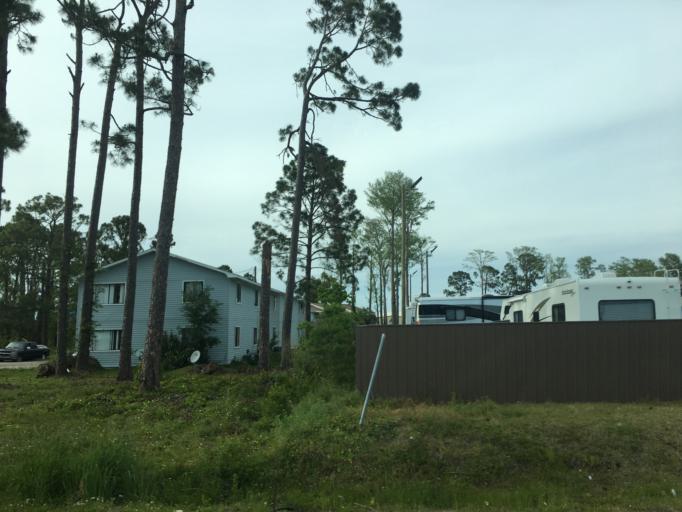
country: US
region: Florida
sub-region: Bay County
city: Upper Grand Lagoon
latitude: 30.1786
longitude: -85.7626
